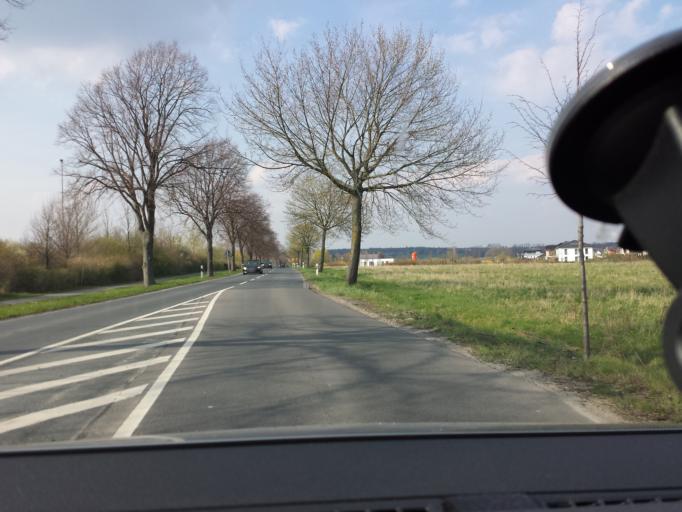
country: DE
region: Lower Saxony
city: Braunschweig
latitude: 52.2627
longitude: 10.4492
